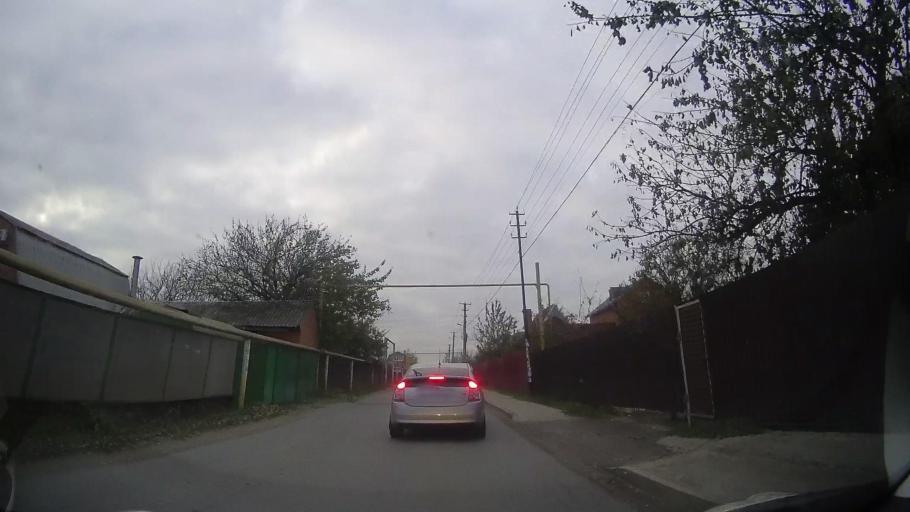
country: RU
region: Rostov
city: Bataysk
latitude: 47.0856
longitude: 39.7610
